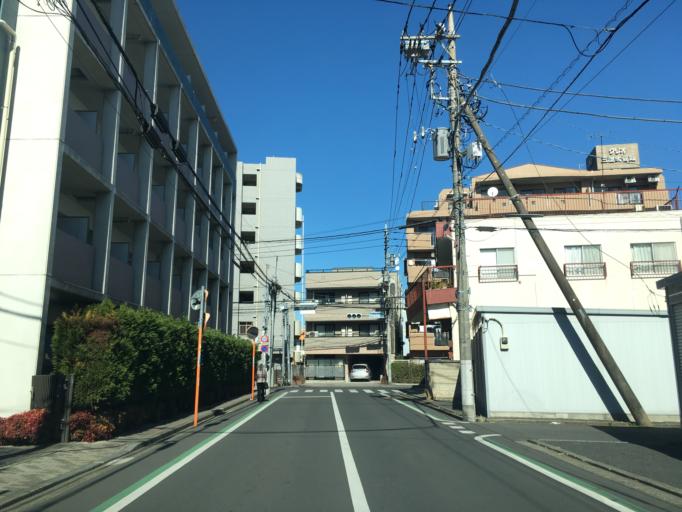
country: JP
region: Tokyo
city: Mitaka-shi
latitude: 35.6833
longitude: 139.5610
